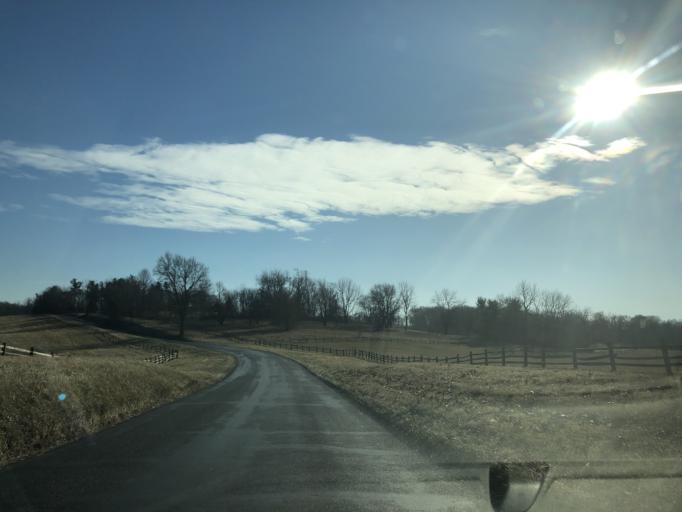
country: US
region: Pennsylvania
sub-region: Chester County
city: Upland
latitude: 39.8984
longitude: -75.7819
